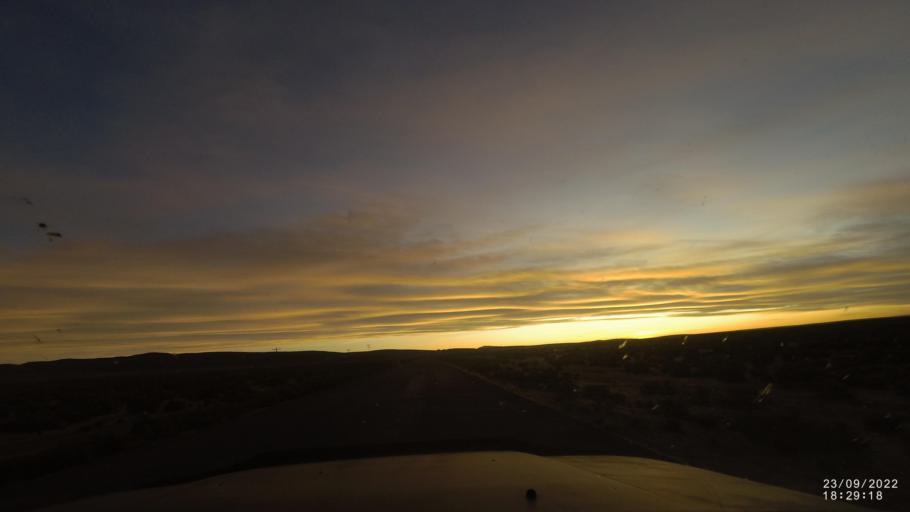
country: BO
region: Oruro
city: Challapata
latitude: -19.3443
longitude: -67.1901
